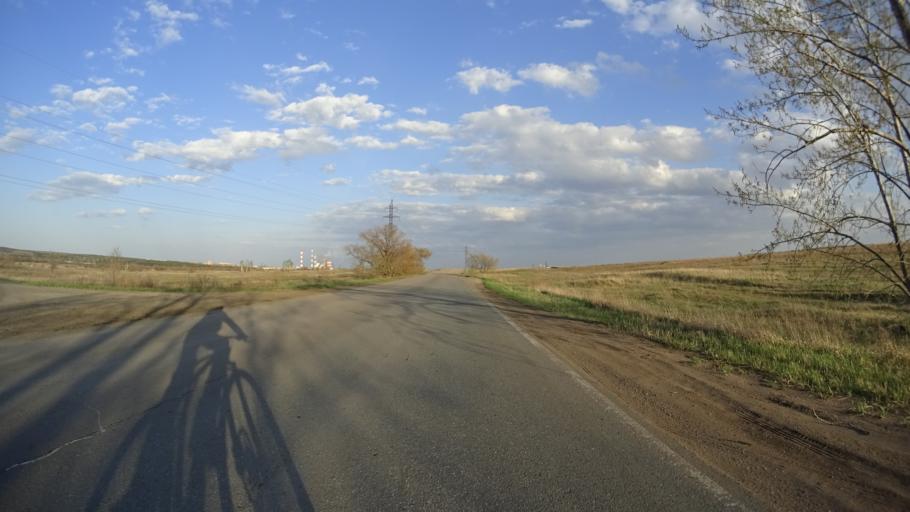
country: RU
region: Chelyabinsk
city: Troitsk
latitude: 54.0536
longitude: 61.5902
